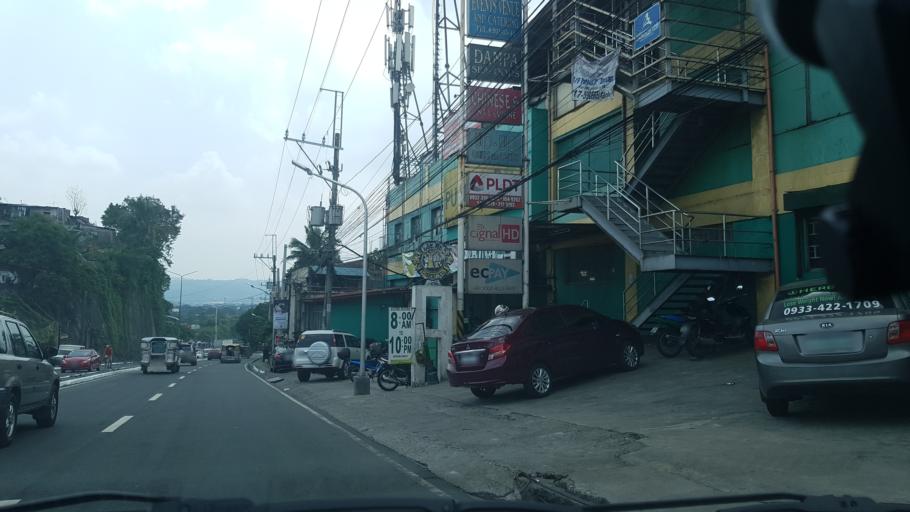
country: PH
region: Calabarzon
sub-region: Province of Rizal
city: San Mateo
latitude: 14.6856
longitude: 121.1026
